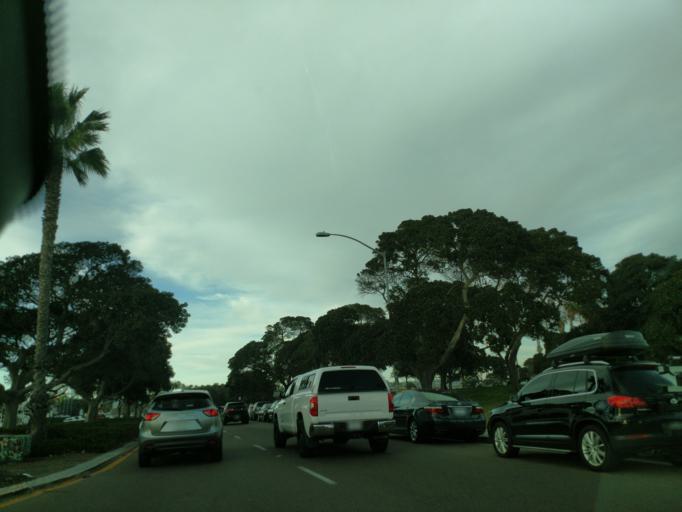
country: US
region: California
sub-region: San Diego County
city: La Jolla
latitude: 32.7699
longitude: -117.2509
